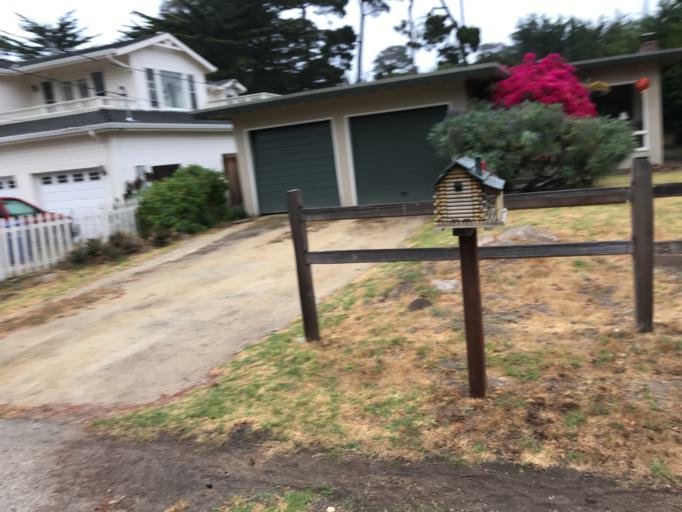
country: US
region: California
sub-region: Monterey County
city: Pacific Grove
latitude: 36.6224
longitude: -121.9363
